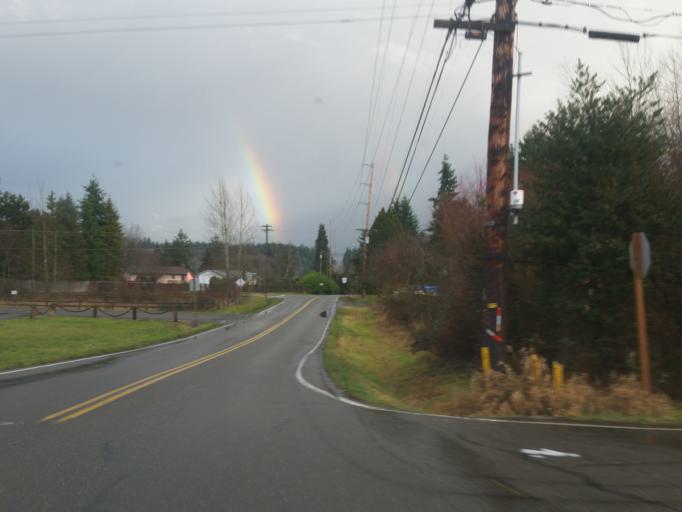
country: US
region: Washington
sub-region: Snohomish County
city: Brier
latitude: 47.7919
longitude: -122.2668
